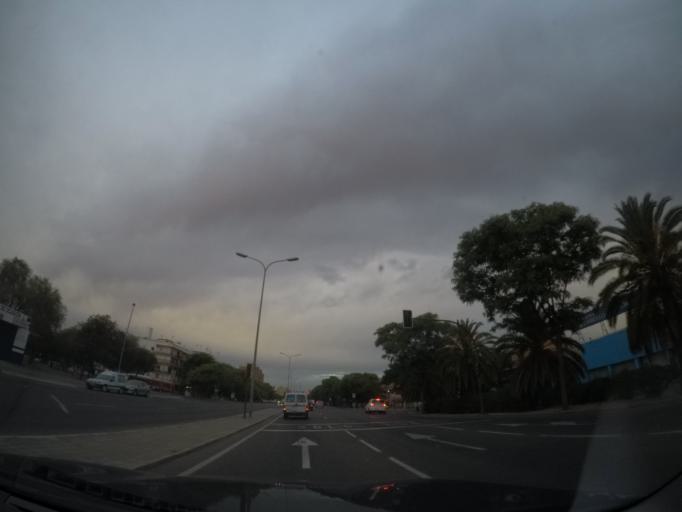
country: ES
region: Andalusia
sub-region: Provincia de Sevilla
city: Sevilla
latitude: 37.3871
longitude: -5.9533
